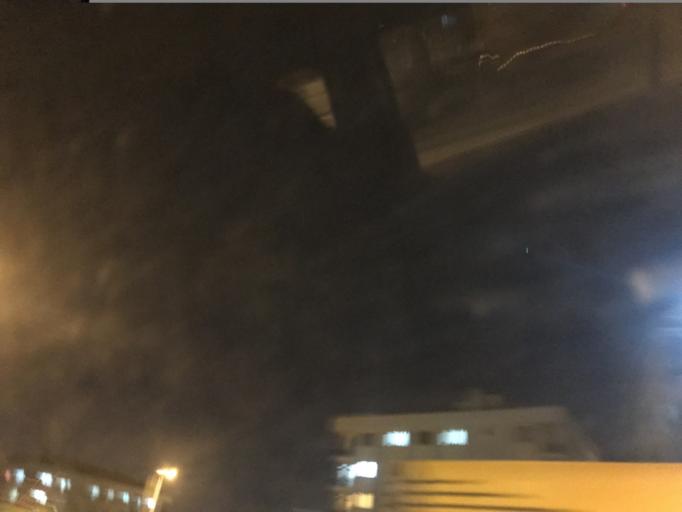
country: TR
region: Istanbul
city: Pendik
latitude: 40.8967
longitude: 29.2552
